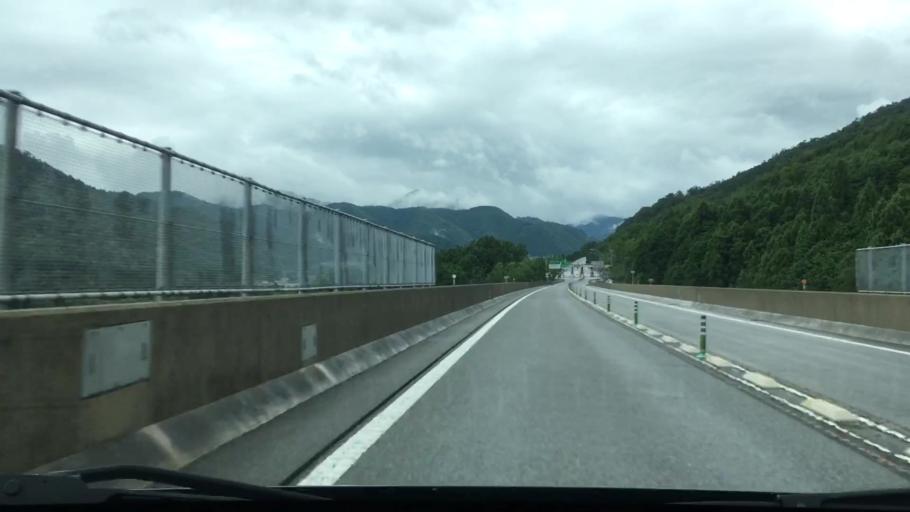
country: JP
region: Hyogo
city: Toyooka
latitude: 35.2908
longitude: 134.8241
